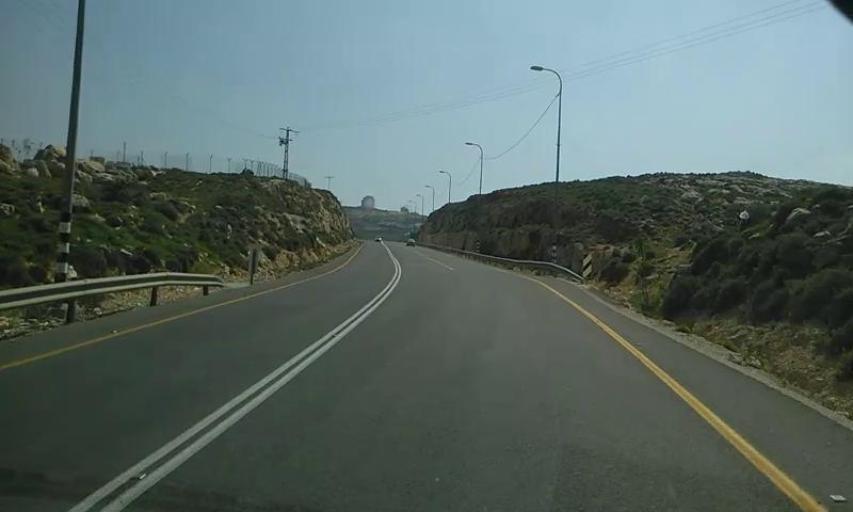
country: PS
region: West Bank
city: Jaba`
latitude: 31.8681
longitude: 35.2582
